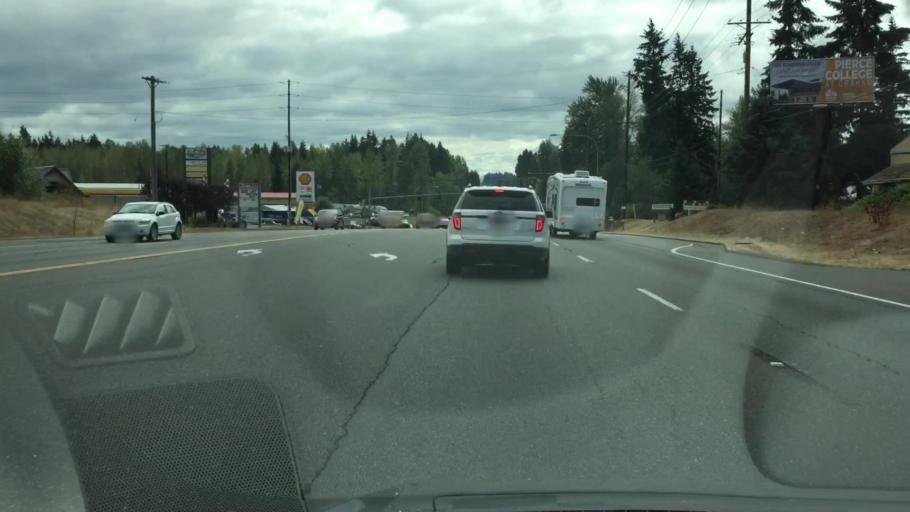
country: US
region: Washington
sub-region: Pierce County
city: Graham
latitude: 47.0764
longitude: -122.2942
